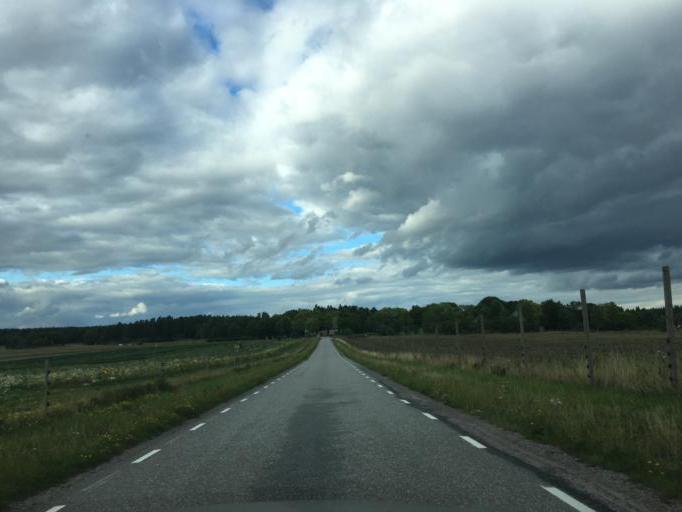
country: SE
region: Vaestmanland
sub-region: Vasteras
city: Tillberga
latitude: 59.5509
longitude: 16.7522
